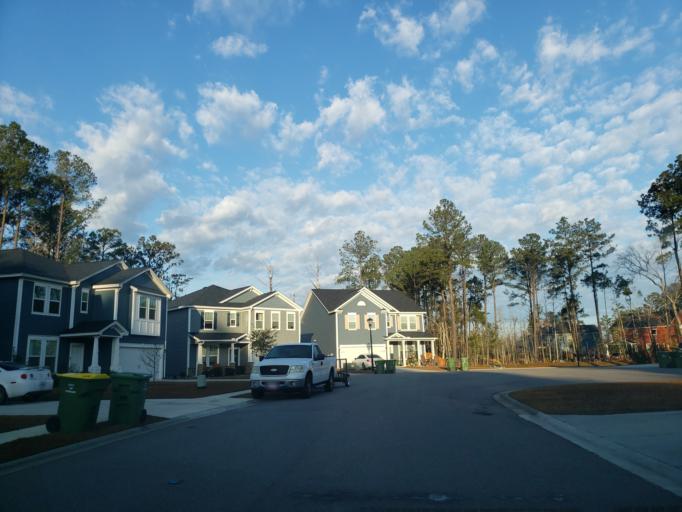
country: US
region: Georgia
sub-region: Chatham County
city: Bloomingdale
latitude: 32.1507
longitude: -81.2754
